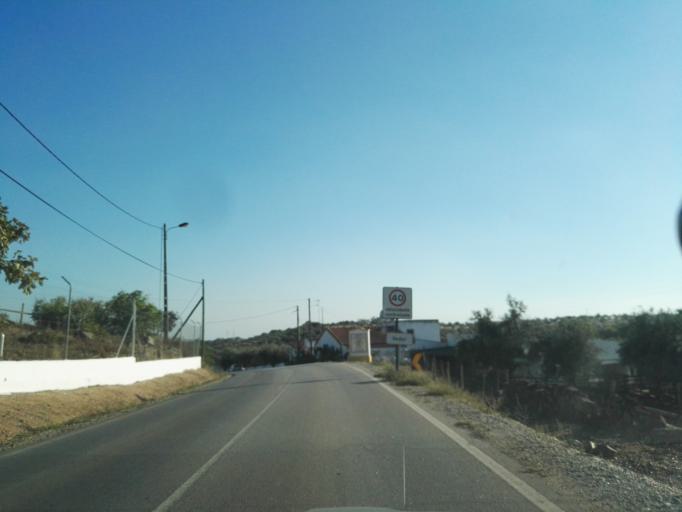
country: PT
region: Portalegre
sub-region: Elvas
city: Elvas
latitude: 38.8985
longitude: -7.1773
